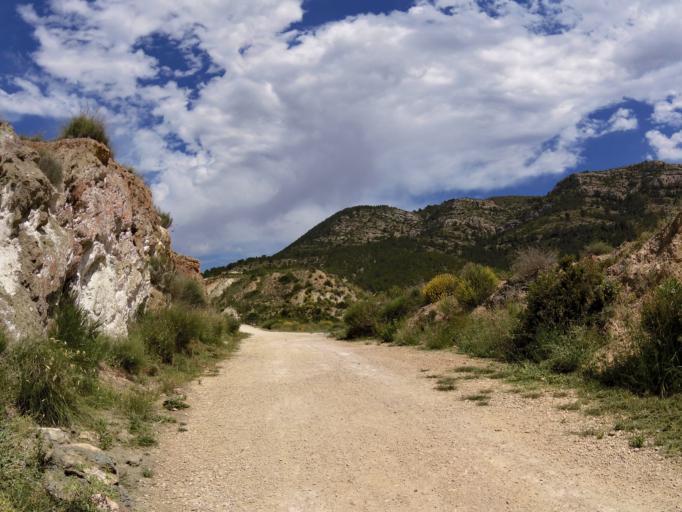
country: ES
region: Valencia
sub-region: Provincia de Alicante
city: Agost
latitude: 38.4830
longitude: -0.6287
